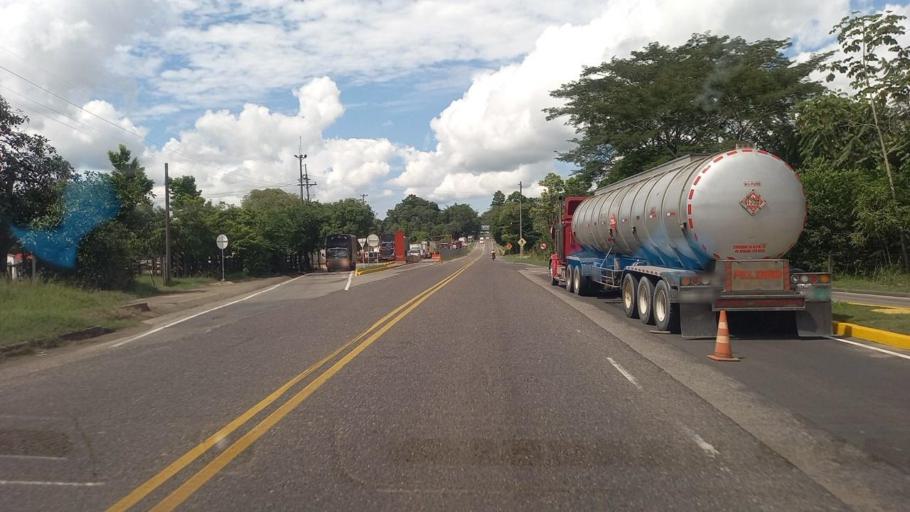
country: CO
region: Santander
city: Barrancabermeja
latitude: 7.1252
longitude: -73.5815
